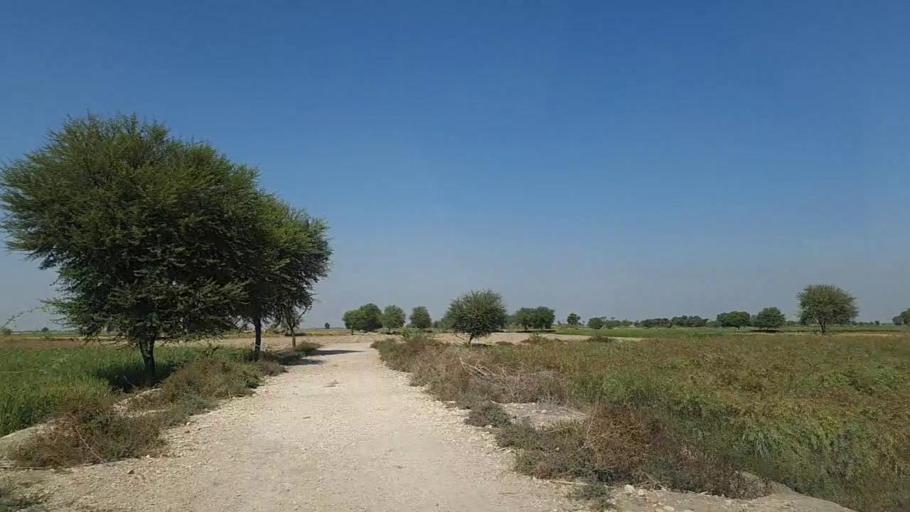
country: PK
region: Sindh
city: Pithoro
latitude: 25.4160
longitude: 69.4078
